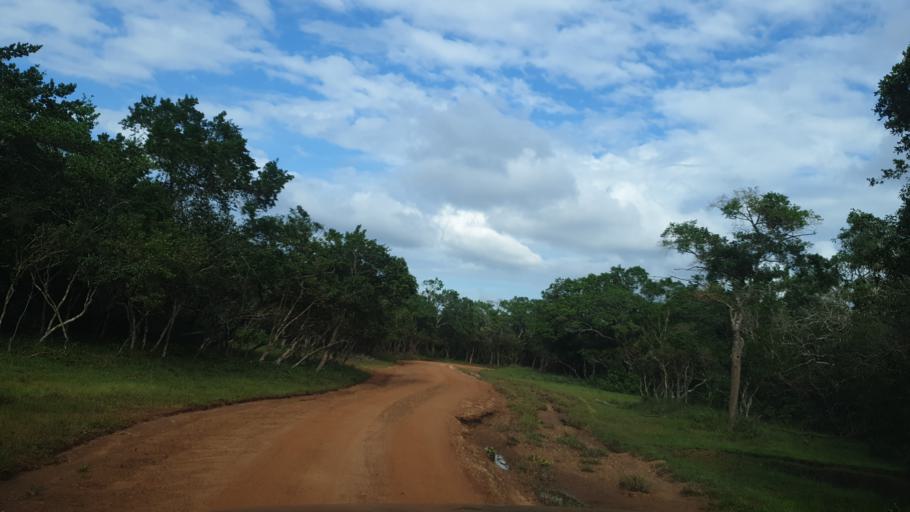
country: LK
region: North Central
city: Anuradhapura
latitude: 8.3628
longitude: 80.0963
